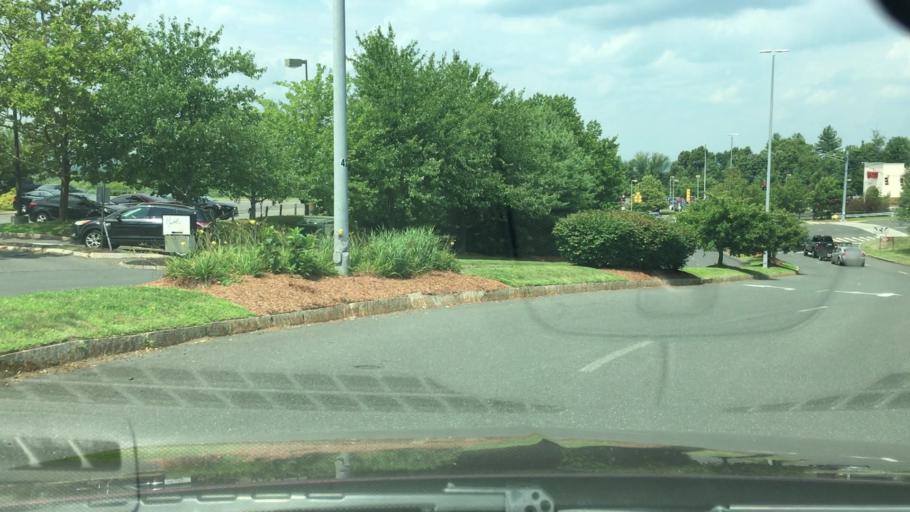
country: US
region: Connecticut
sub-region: Hartford County
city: Manchester
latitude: 41.8079
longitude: -72.5498
